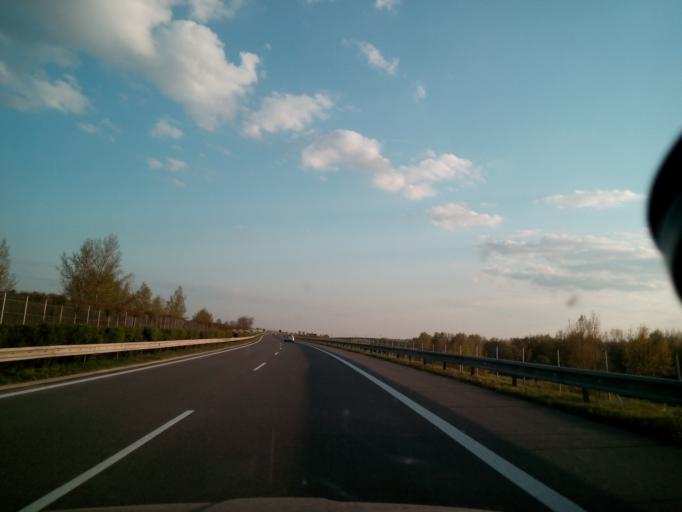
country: SK
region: Trenciansky
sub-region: Okres Nove Mesto nad Vahom
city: Nove Mesto nad Vahom
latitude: 48.7955
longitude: 17.8899
